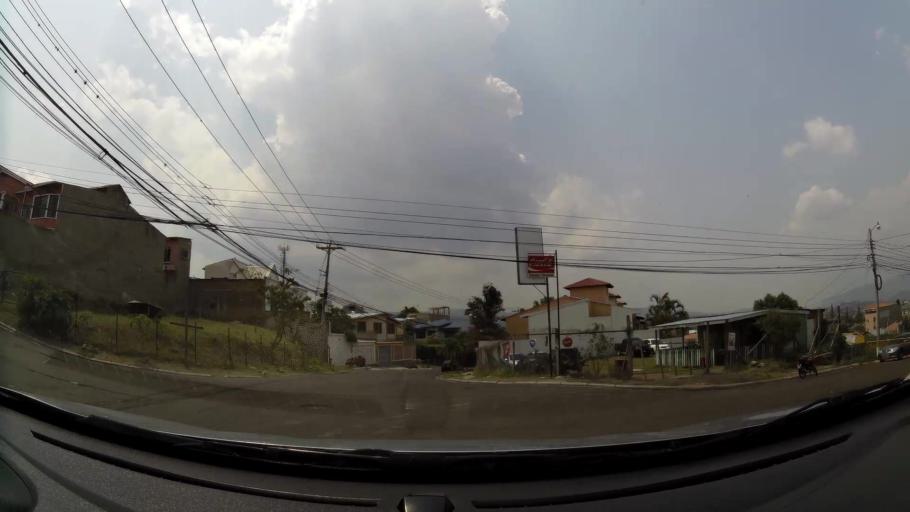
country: HN
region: Francisco Morazan
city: Yaguacire
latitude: 14.0444
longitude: -87.2324
